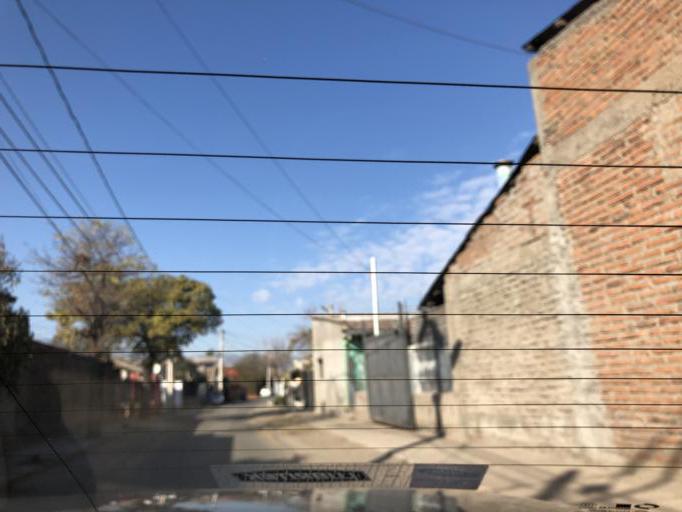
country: CL
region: Santiago Metropolitan
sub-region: Provincia de Cordillera
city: Puente Alto
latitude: -33.6184
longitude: -70.5828
